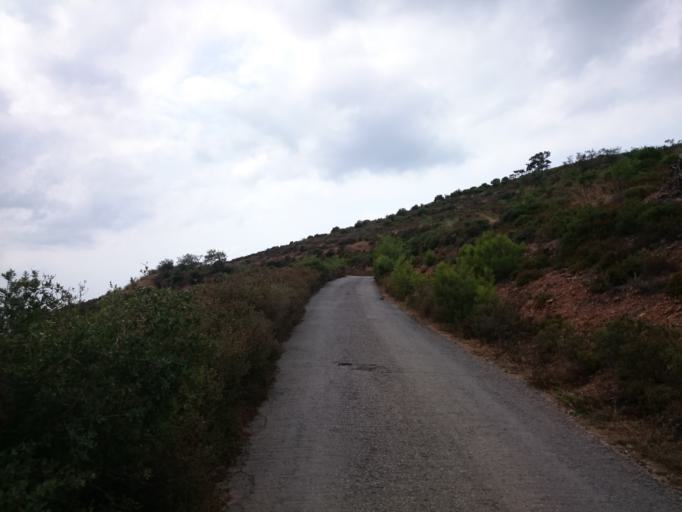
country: TR
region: Istanbul
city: Adalan
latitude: 40.8751
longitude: 29.0647
